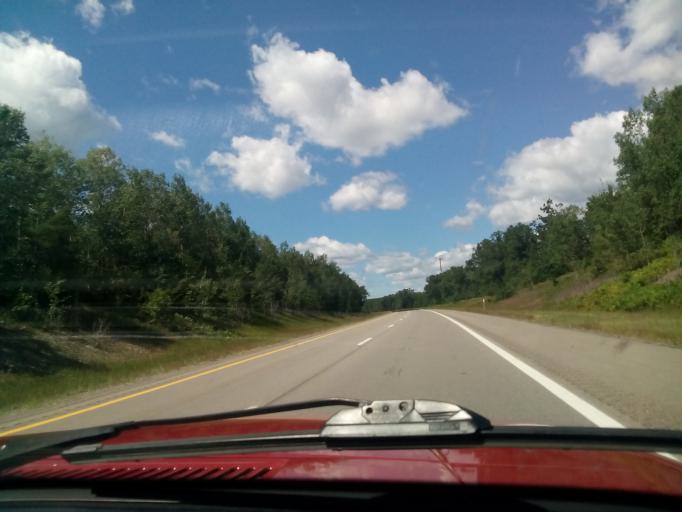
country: US
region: Michigan
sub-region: Roscommon County
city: Roscommon
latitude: 44.4724
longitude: -84.6176
